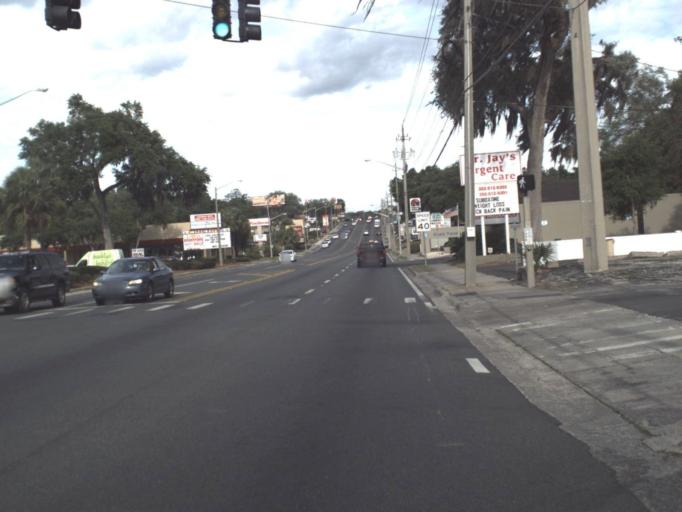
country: US
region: Florida
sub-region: Marion County
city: Ocala
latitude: 29.1869
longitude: -82.1116
